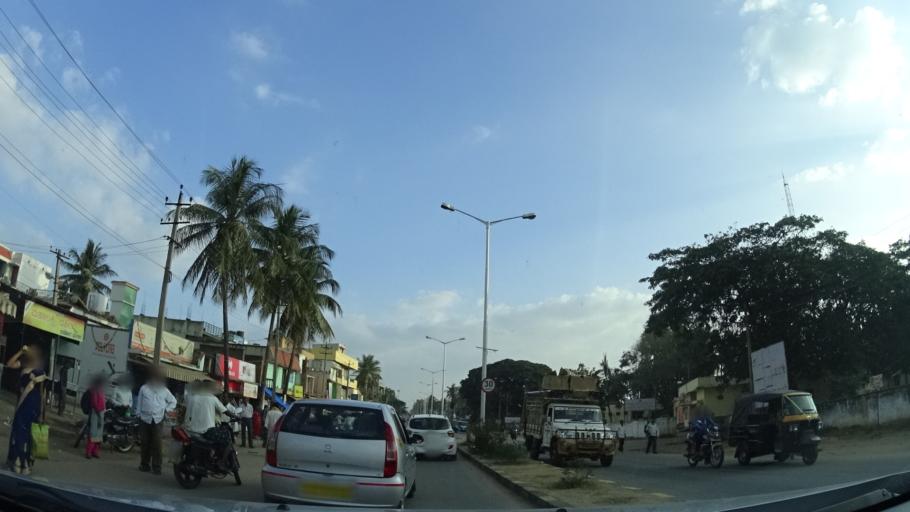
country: IN
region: Karnataka
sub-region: Mandya
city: Malavalli
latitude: 12.3842
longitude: 77.0605
